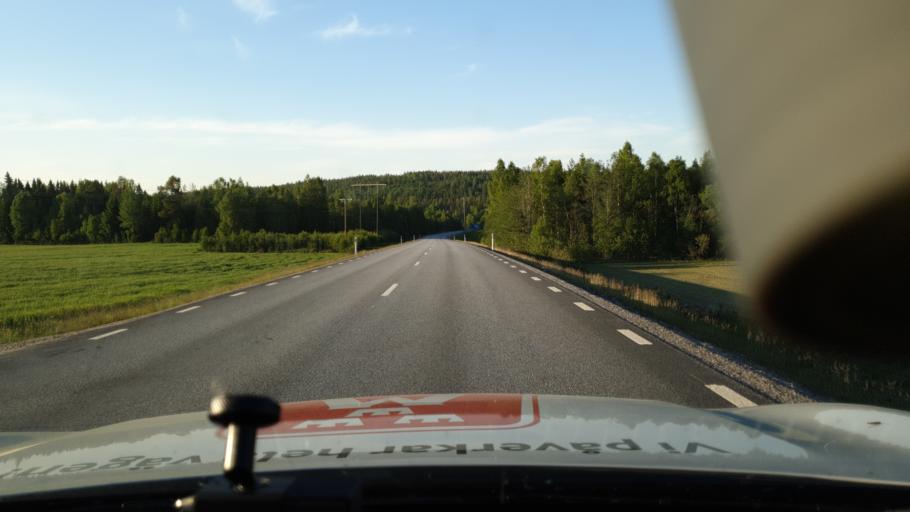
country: SE
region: Vaesterbotten
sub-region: Vannas Kommun
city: Vaennaes
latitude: 63.9064
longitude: 19.6980
